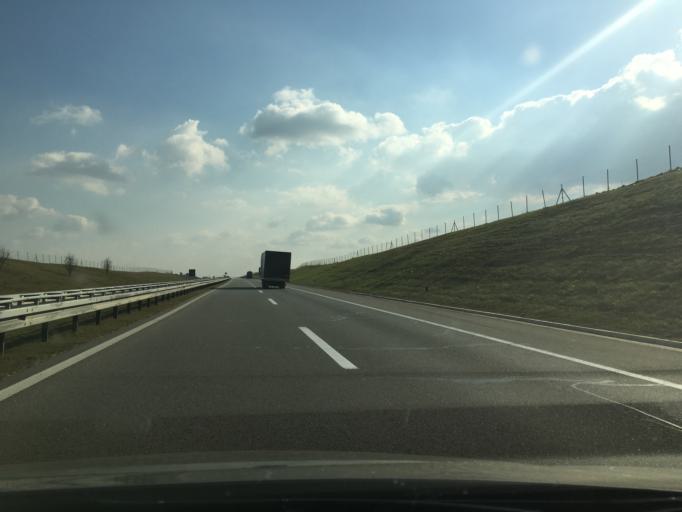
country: RS
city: Beska
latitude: 45.1225
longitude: 20.0945
